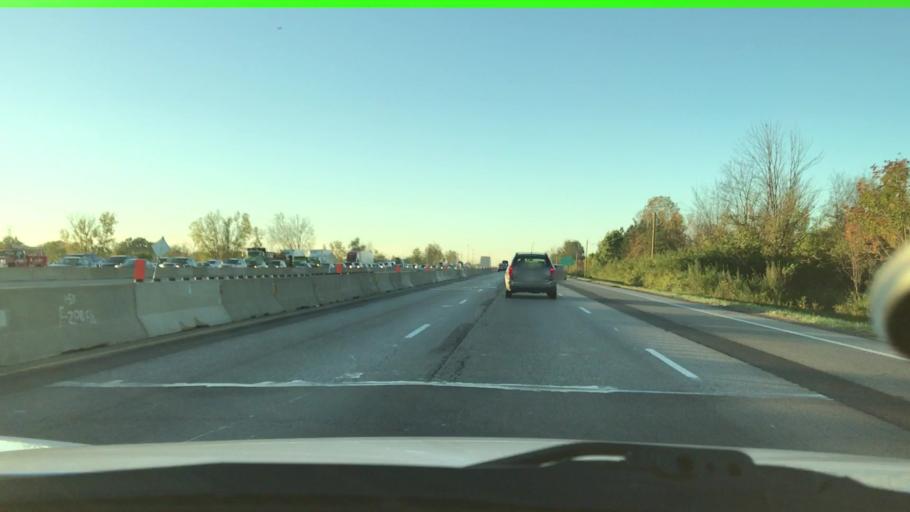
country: US
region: Ohio
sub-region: Franklin County
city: Hilliard
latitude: 40.0483
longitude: -83.1282
